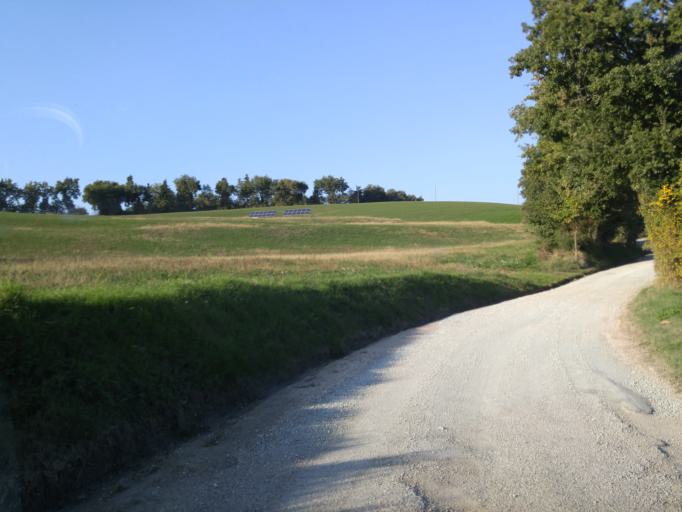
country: IT
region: The Marches
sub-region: Provincia di Pesaro e Urbino
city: Fossombrone
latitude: 43.7102
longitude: 12.8150
